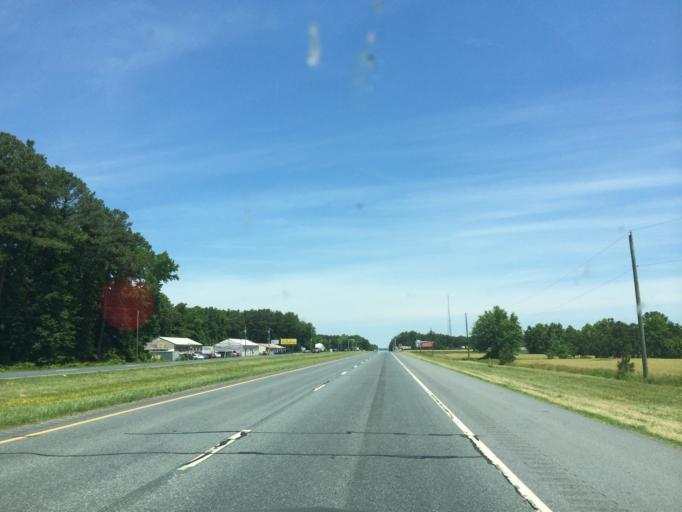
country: US
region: Delaware
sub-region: Sussex County
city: Delmar
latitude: 38.4966
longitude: -75.5573
